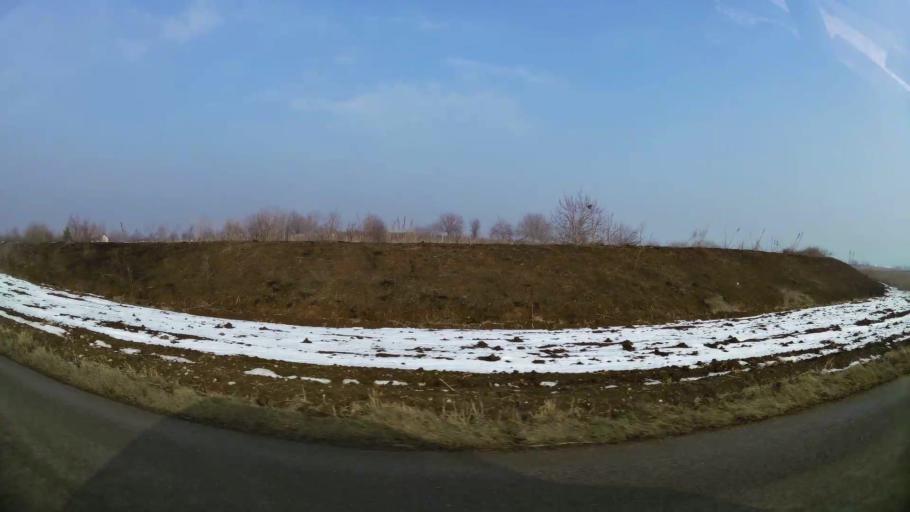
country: MK
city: Kadino
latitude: 41.9731
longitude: 21.6049
